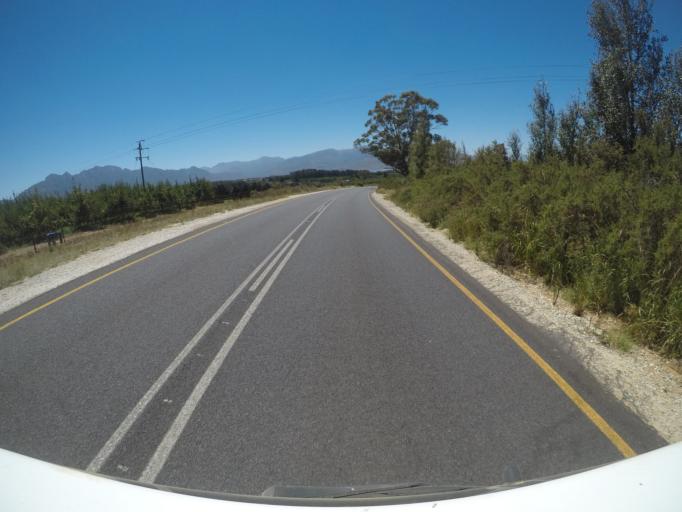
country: ZA
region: Western Cape
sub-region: Overberg District Municipality
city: Grabouw
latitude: -34.0602
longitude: 19.1364
